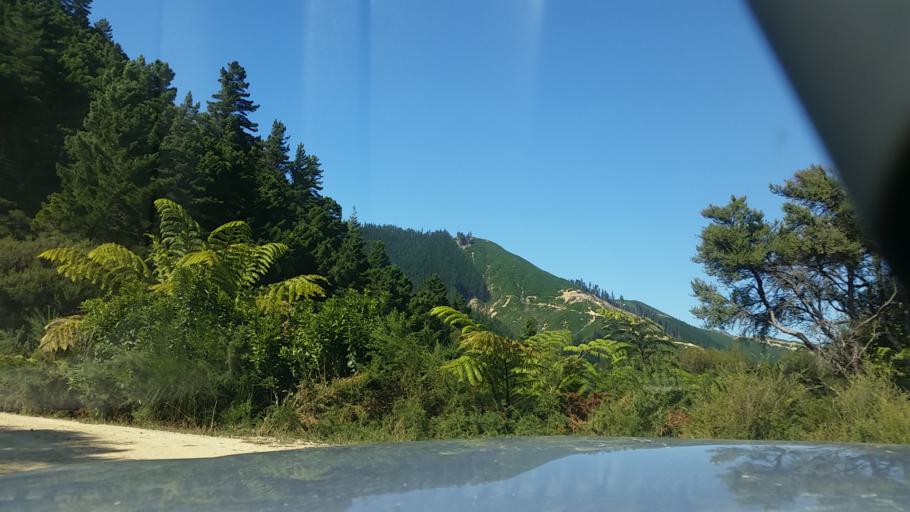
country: NZ
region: Marlborough
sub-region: Marlborough District
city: Picton
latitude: -41.3079
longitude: 174.1714
